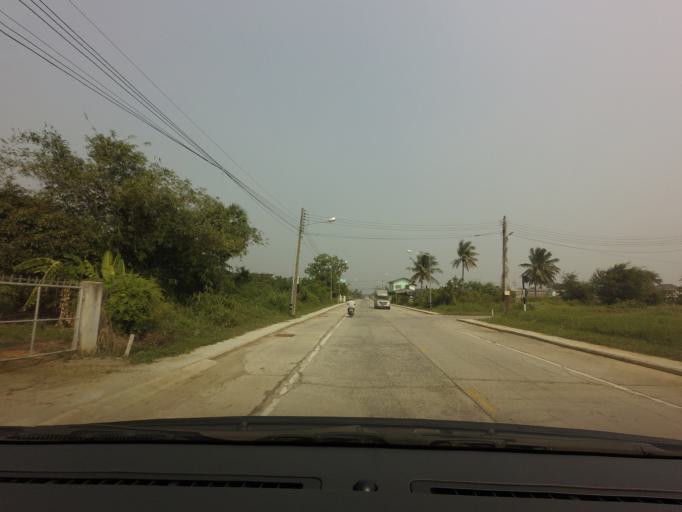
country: TH
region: Prachuap Khiri Khan
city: Kui Buri
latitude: 12.0700
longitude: 99.8638
